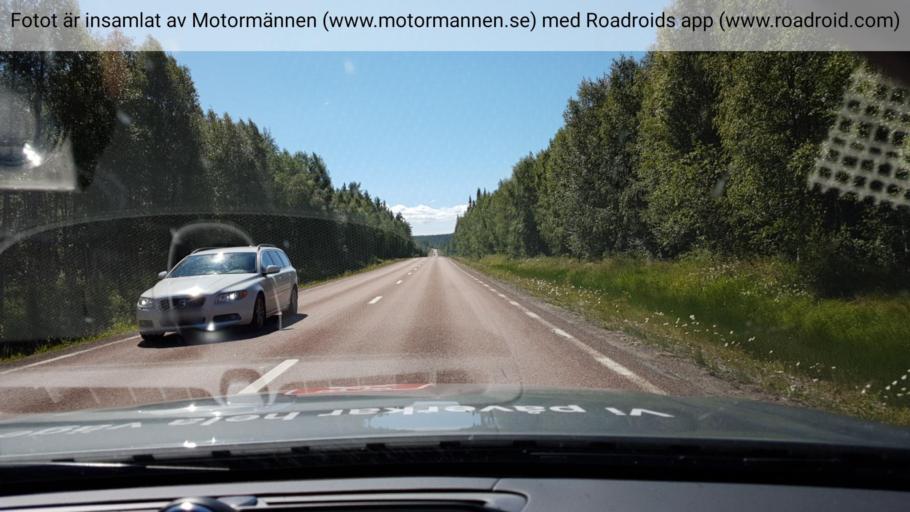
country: SE
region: Jaemtland
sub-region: Stroemsunds Kommun
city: Stroemsund
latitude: 63.9010
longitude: 15.7169
